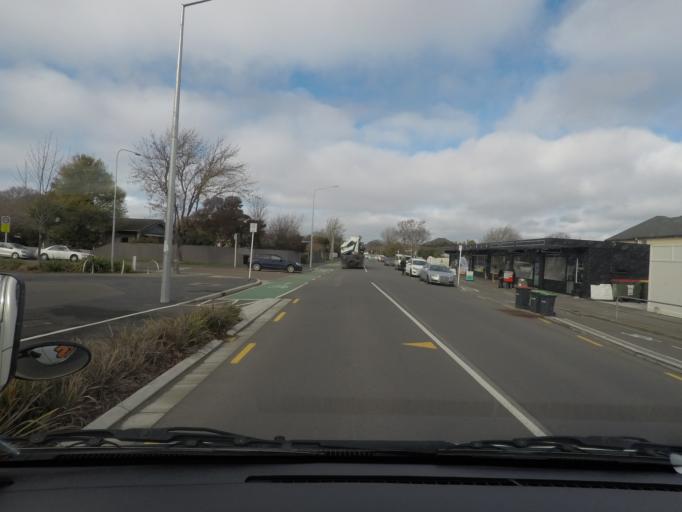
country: NZ
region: Canterbury
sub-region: Christchurch City
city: Christchurch
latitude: -43.5062
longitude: 172.6285
